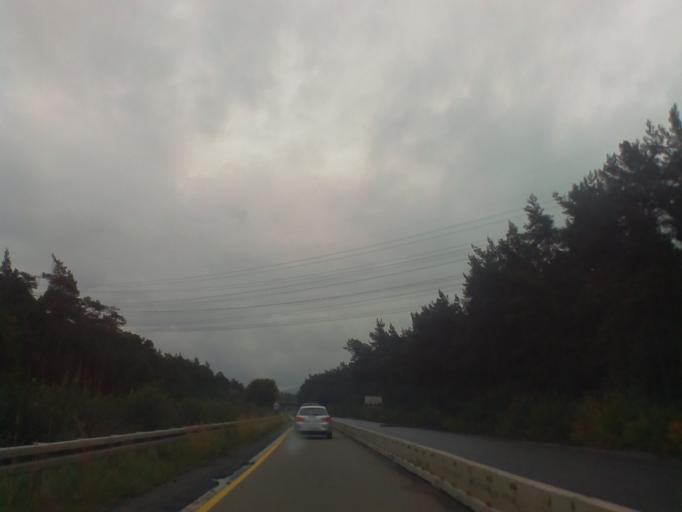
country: DE
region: Hesse
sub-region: Regierungsbezirk Darmstadt
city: Grosskrotzenburg
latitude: 50.1071
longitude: 9.0012
